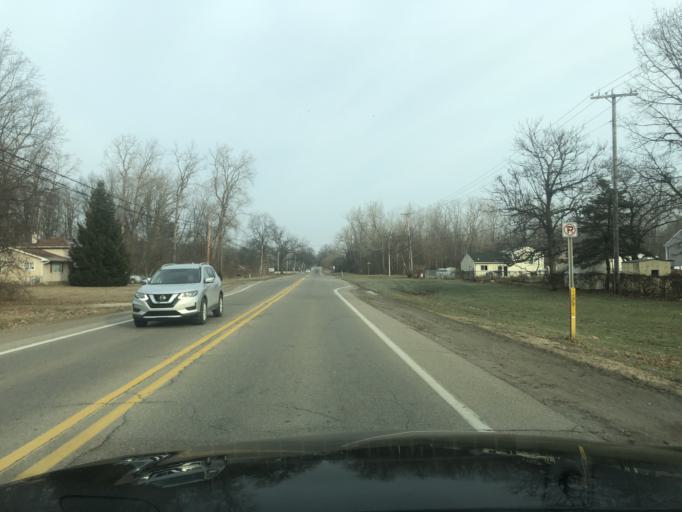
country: US
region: Michigan
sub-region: Wayne County
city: Taylor
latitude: 42.1871
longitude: -83.3257
